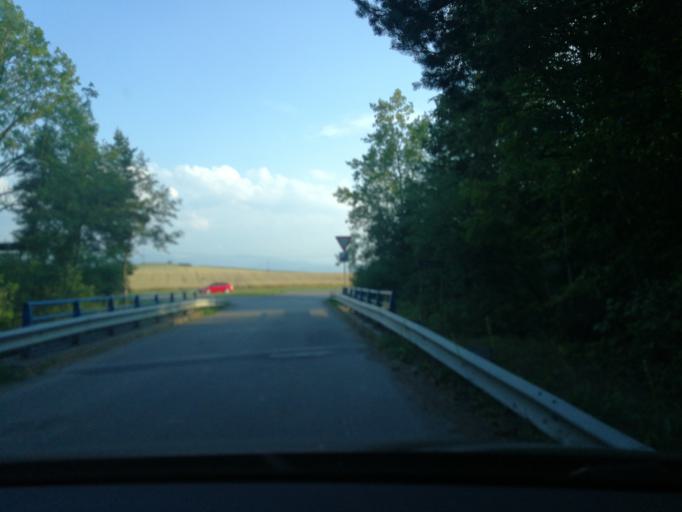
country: SK
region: Zilinsky
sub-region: Okres Liptovsky Mikulas
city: Liptovsky Mikulas
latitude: 49.1523
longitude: 19.5296
